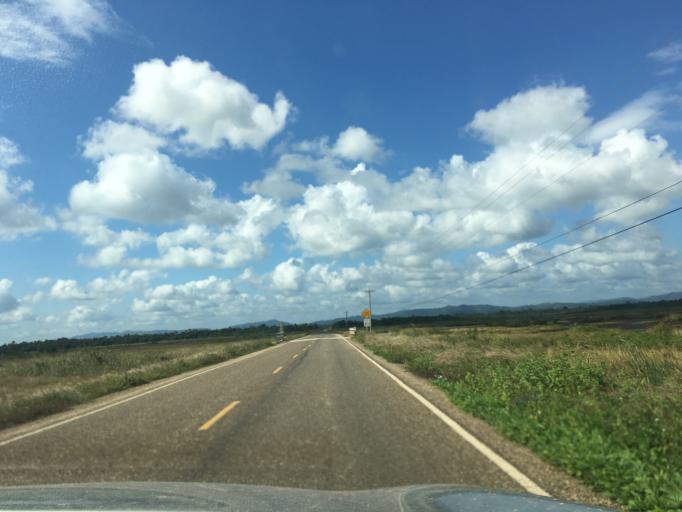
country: BZ
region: Stann Creek
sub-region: Dangriga
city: Dangriga
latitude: 16.8610
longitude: -88.2930
